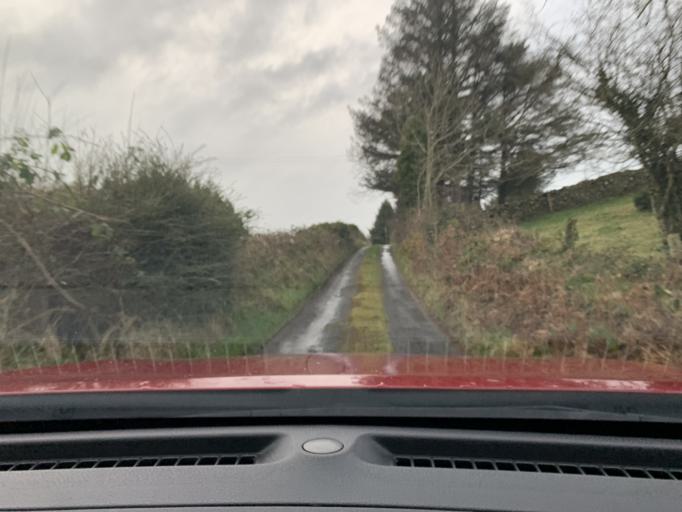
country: IE
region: Connaught
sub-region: Roscommon
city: Boyle
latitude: 53.9806
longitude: -8.4199
